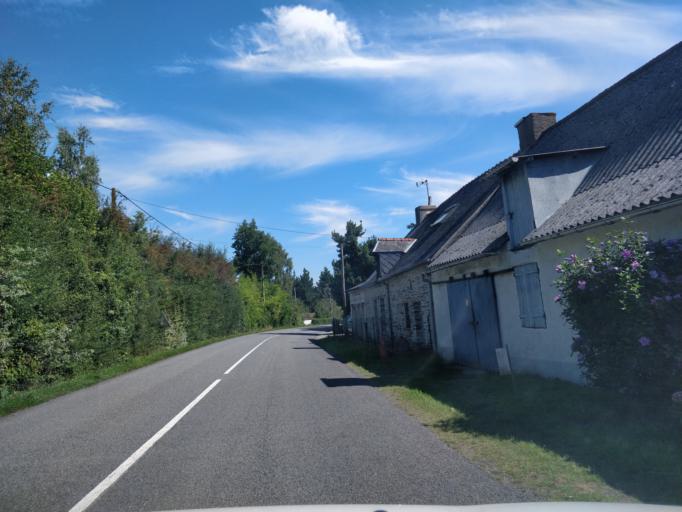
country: FR
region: Pays de la Loire
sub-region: Departement de la Loire-Atlantique
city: Conquereuil
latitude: 47.6728
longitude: -1.7722
